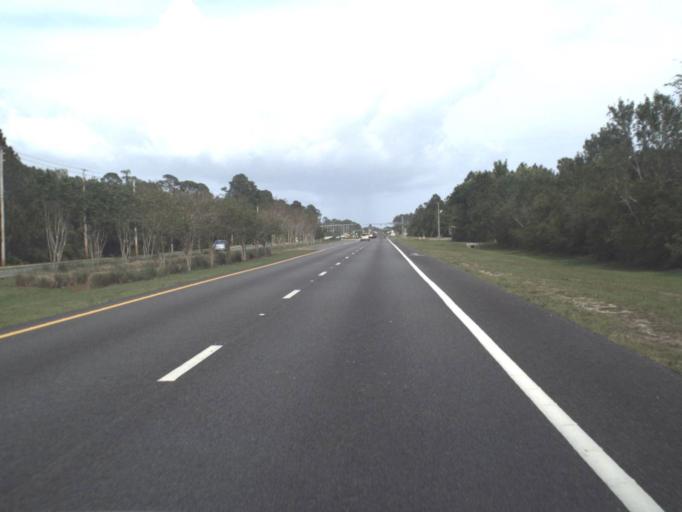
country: US
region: Florida
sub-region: Flagler County
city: Flagler Beach
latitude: 29.4765
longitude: -81.1586
